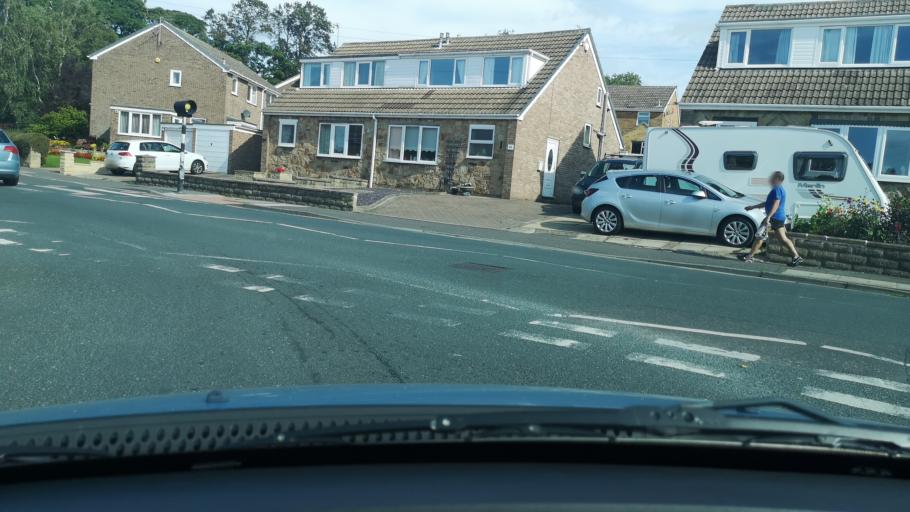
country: GB
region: England
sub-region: City and Borough of Wakefield
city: Ossett
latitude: 53.6707
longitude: -1.5748
